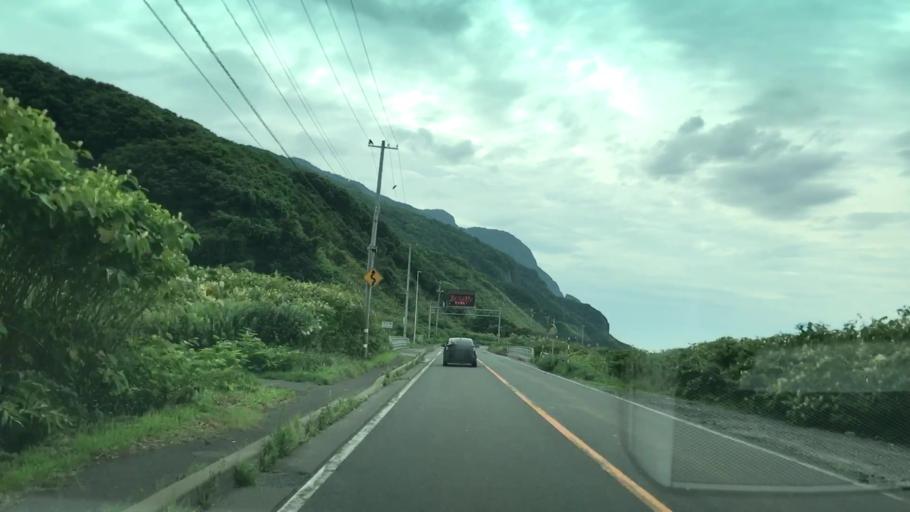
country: JP
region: Hokkaido
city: Iwanai
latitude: 42.9637
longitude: 140.4668
